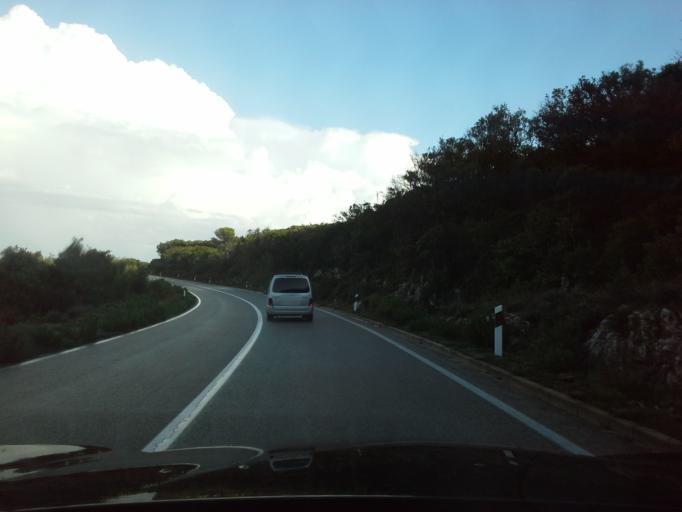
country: HR
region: Primorsko-Goranska
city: Mali Losinj
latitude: 44.6116
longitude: 14.3981
